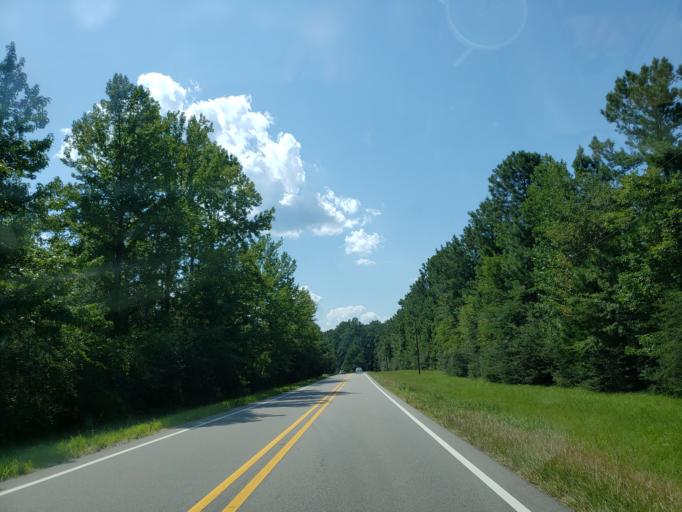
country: US
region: Mississippi
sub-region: Lamar County
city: Sumrall
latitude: 31.3783
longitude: -89.5149
